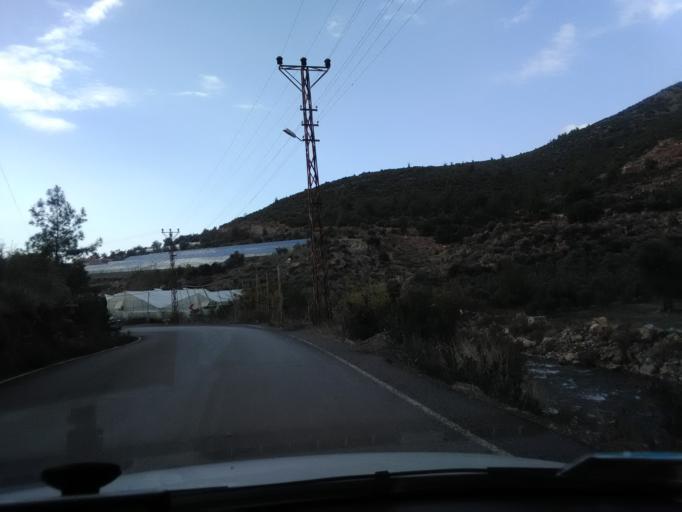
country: TR
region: Antalya
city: Gazipasa
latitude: 36.2775
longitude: 32.3563
